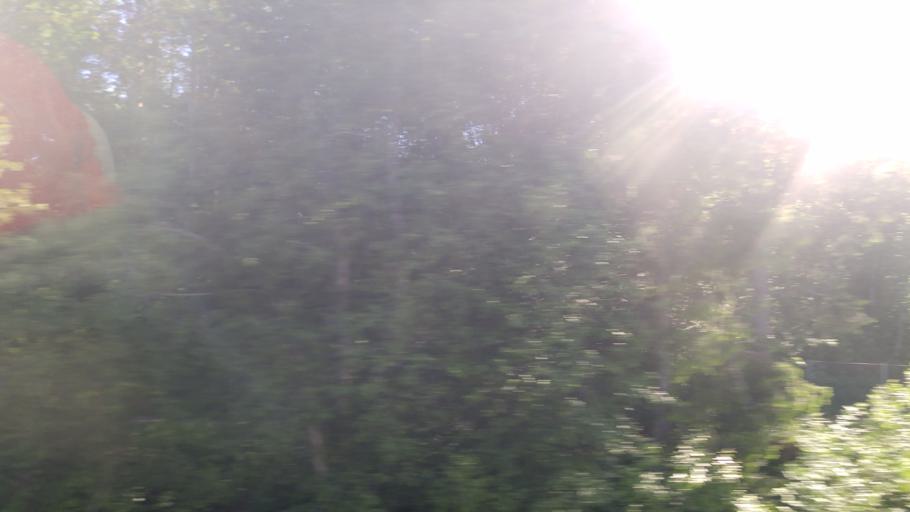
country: NO
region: Sor-Trondelag
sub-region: Trondheim
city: Trondheim
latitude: 63.3736
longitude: 10.3594
